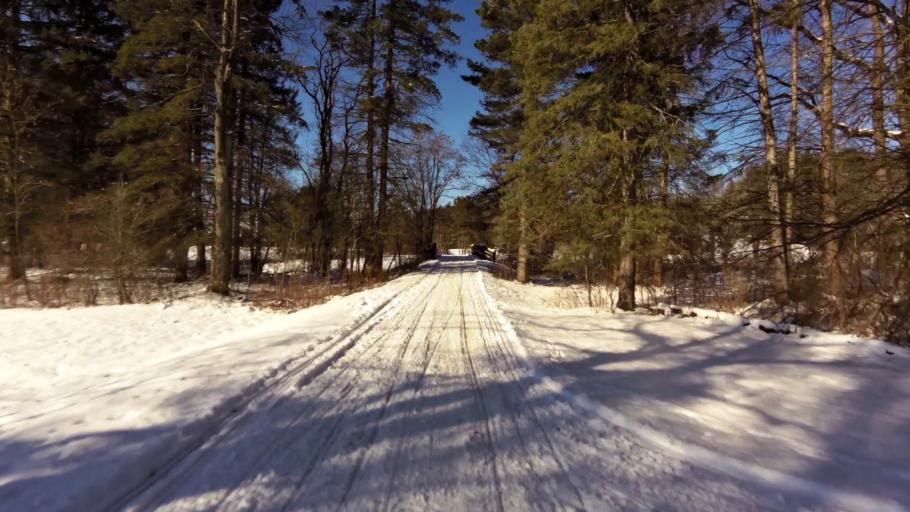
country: US
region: New York
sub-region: Cattaraugus County
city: Salamanca
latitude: 42.1063
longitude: -78.7440
